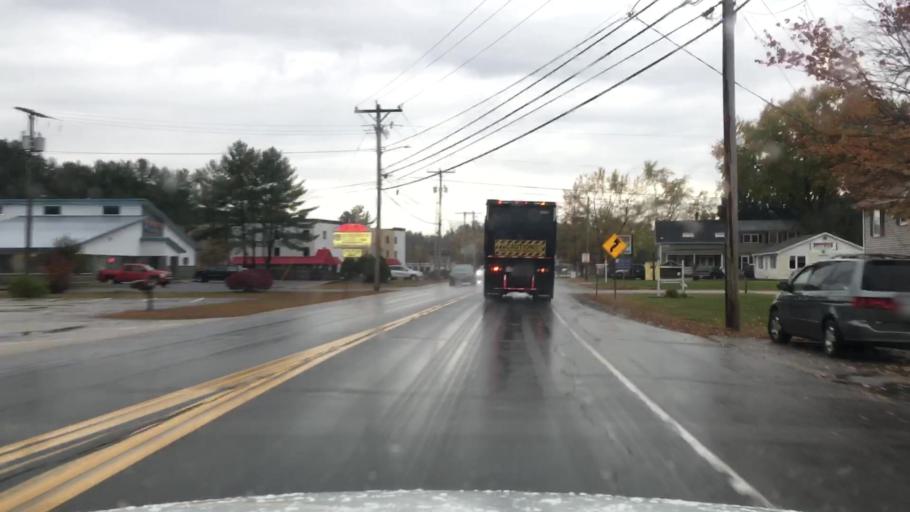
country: US
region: New Hampshire
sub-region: Strafford County
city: Somersworth
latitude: 43.2467
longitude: -70.8997
